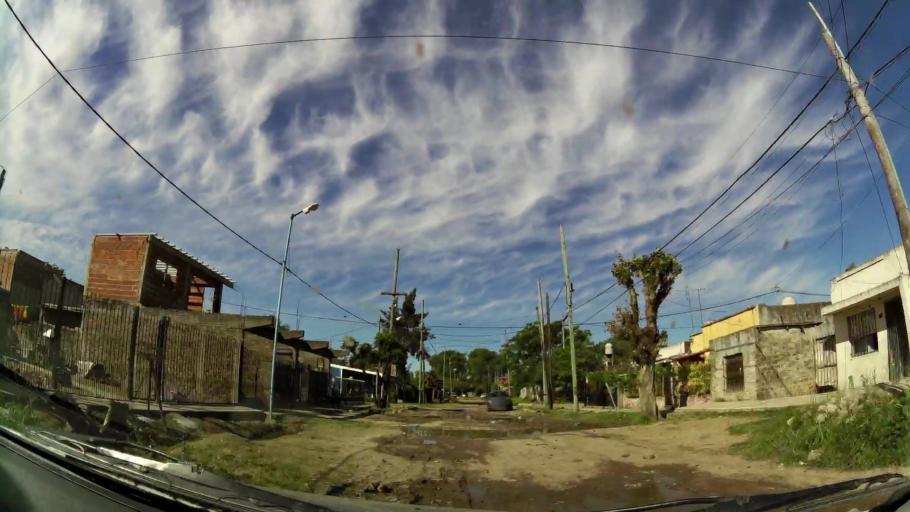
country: AR
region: Buenos Aires
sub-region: Partido de Quilmes
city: Quilmes
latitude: -34.7660
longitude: -58.3027
